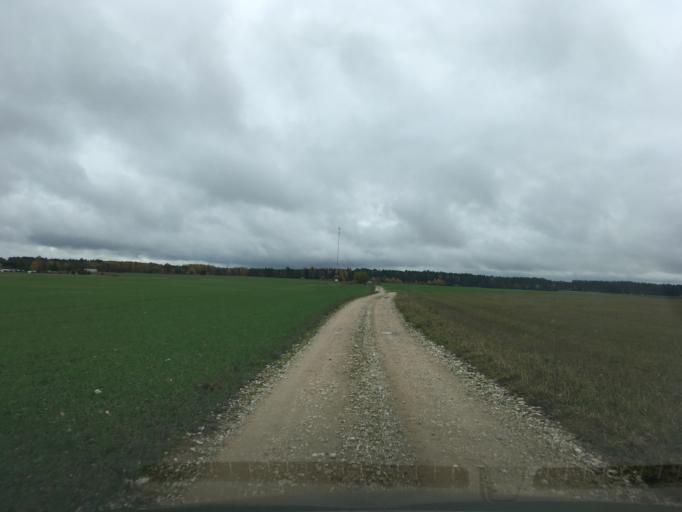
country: EE
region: Harju
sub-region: Raasiku vald
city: Raasiku
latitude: 59.1826
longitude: 25.1484
